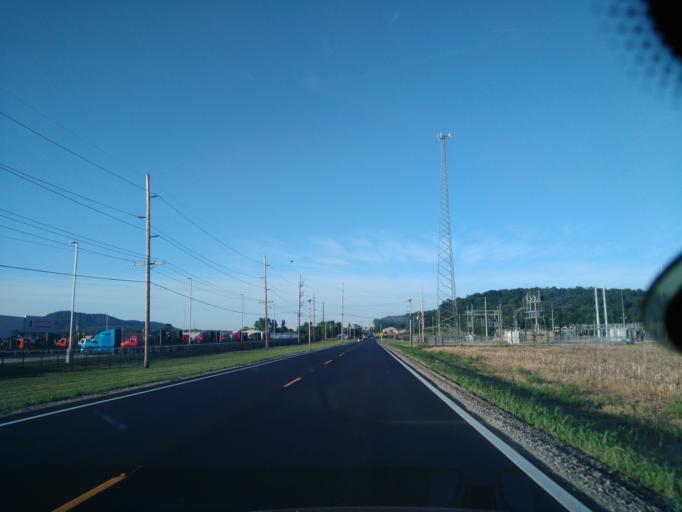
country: US
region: Ohio
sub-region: Ross County
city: Kingston
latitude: 39.4099
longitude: -82.9588
